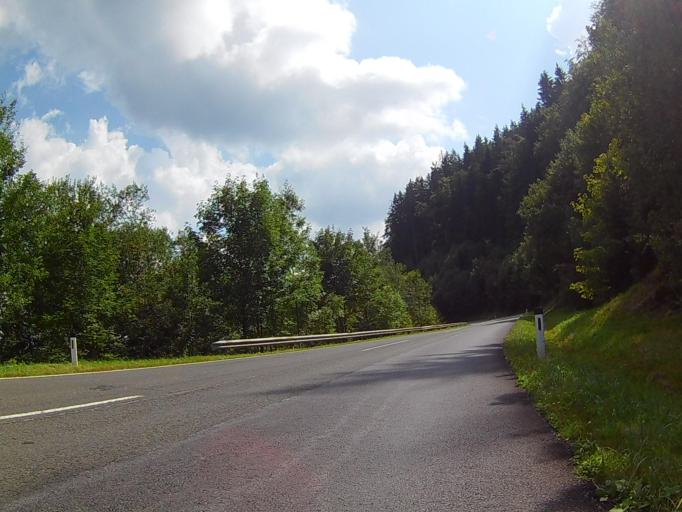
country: AT
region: Styria
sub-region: Politischer Bezirk Deutschlandsberg
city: Soboth
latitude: 46.6991
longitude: 15.0978
